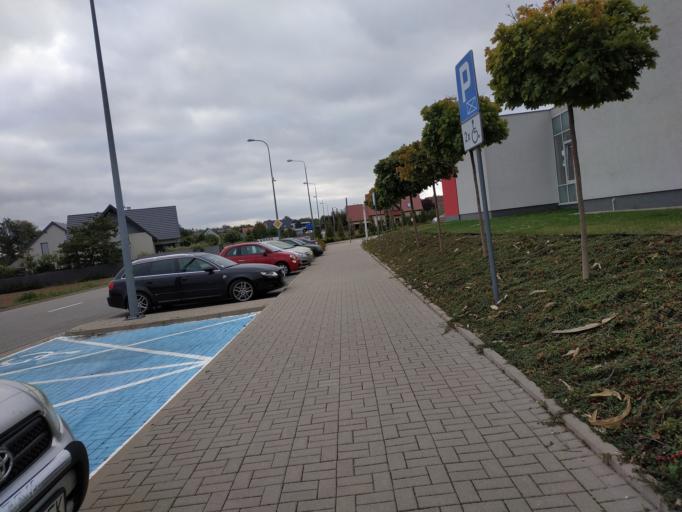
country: PL
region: Lower Silesian Voivodeship
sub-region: Powiat wroclawski
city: Tyniec Maly
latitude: 51.0218
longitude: 16.9104
